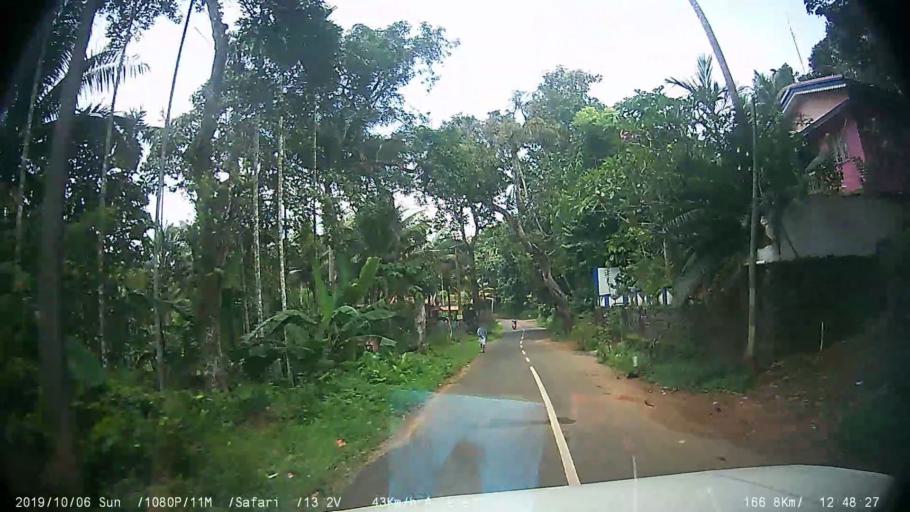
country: IN
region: Kerala
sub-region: Kottayam
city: Palackattumala
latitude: 9.7793
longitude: 76.5973
